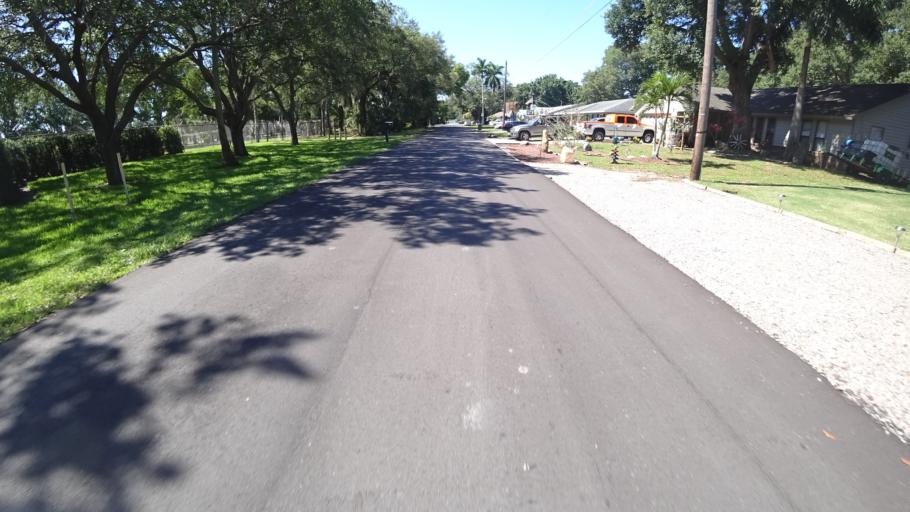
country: US
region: Florida
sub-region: Manatee County
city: West Bradenton
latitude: 27.4914
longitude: -82.5971
